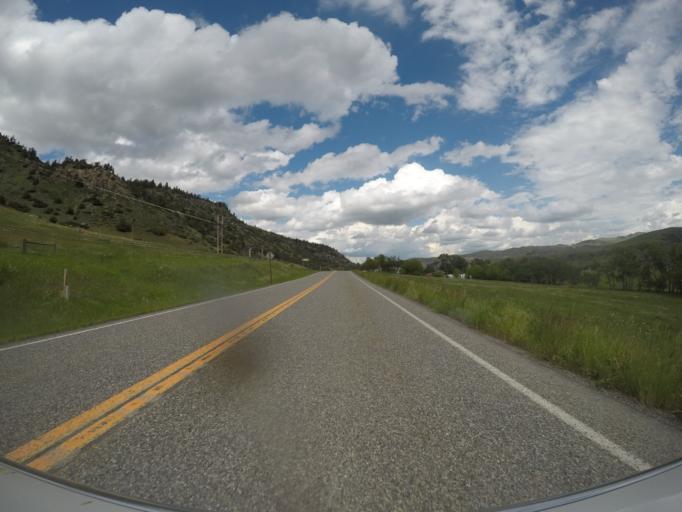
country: US
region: Montana
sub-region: Sweet Grass County
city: Big Timber
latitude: 45.6674
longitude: -110.1090
